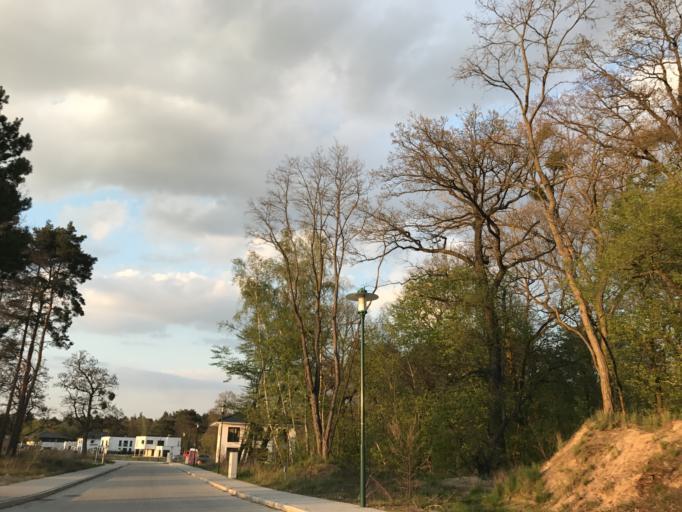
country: DE
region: Berlin
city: Kladow
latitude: 52.4810
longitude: 13.1270
